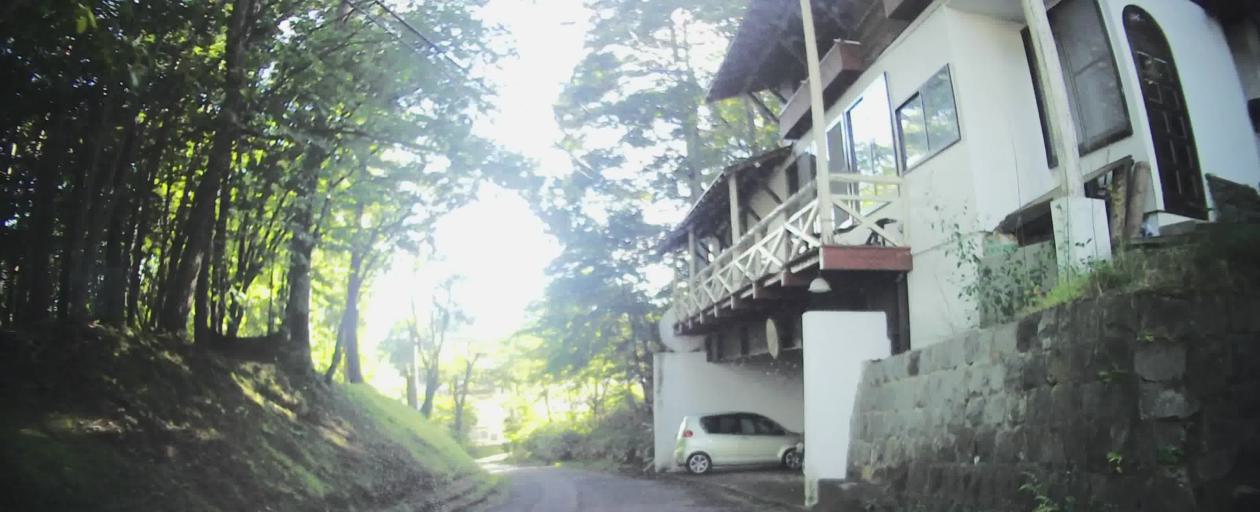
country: JP
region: Gunma
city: Nakanojomachi
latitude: 36.6281
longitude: 138.5998
